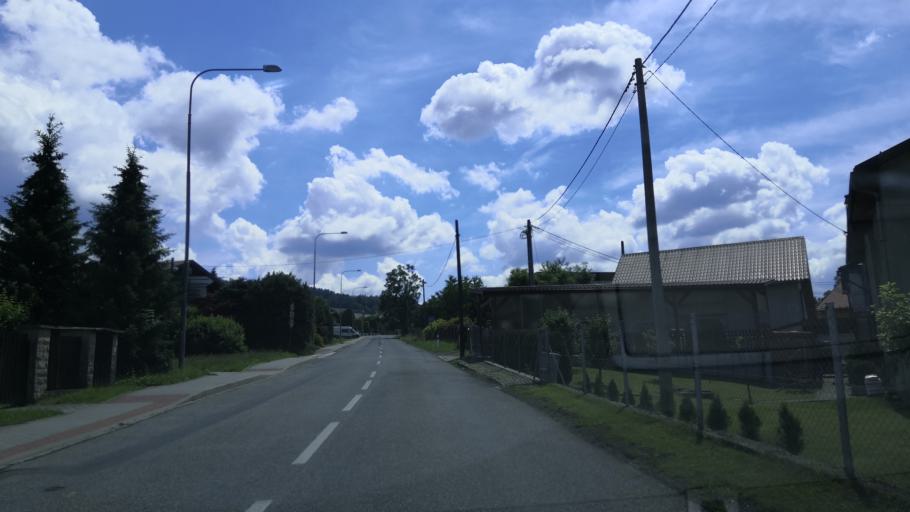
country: CZ
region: Zlin
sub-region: Okres Vsetin
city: Roznov pod Radhostem
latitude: 49.4558
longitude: 18.1448
